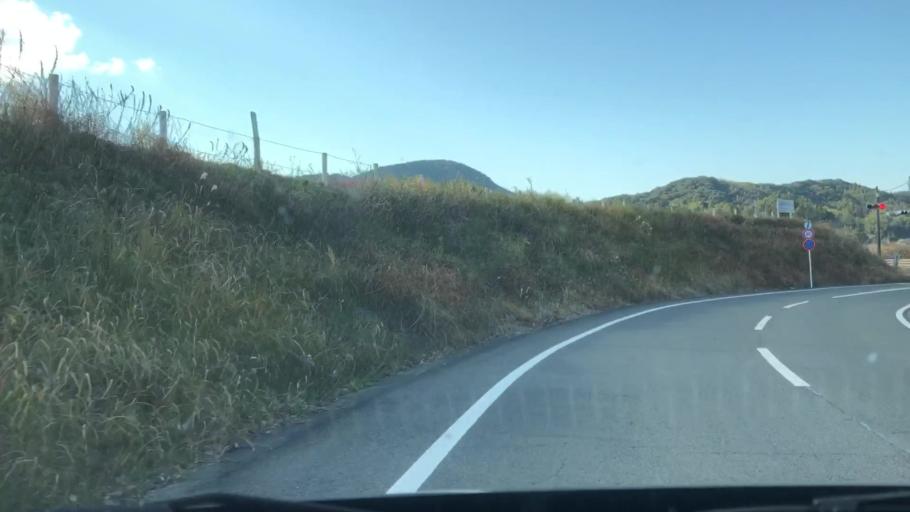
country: JP
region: Kagoshima
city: Satsumasendai
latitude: 31.8649
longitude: 130.3297
